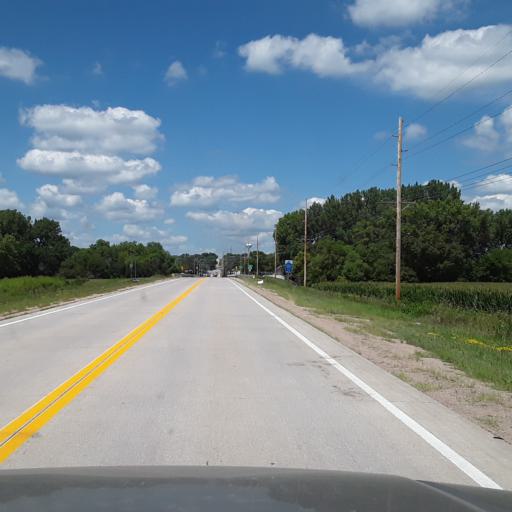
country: US
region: Nebraska
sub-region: Nance County
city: Genoa
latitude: 41.4390
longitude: -97.7346
